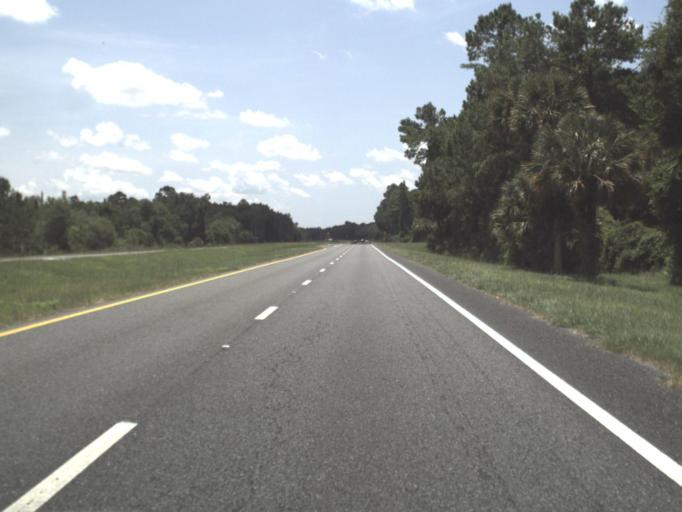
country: US
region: Florida
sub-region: Taylor County
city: Steinhatchee
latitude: 29.7576
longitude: -83.3222
